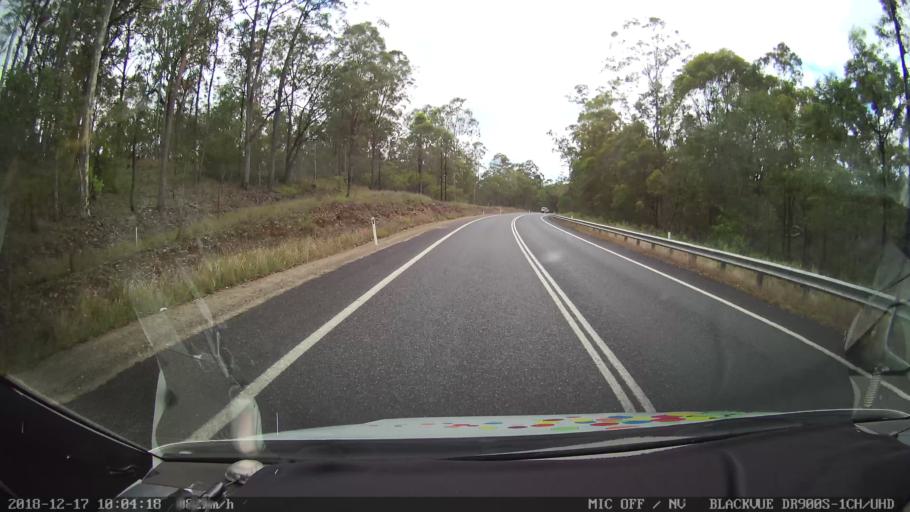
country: AU
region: New South Wales
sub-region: Tenterfield Municipality
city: Carrolls Creek
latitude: -28.8938
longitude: 152.4754
